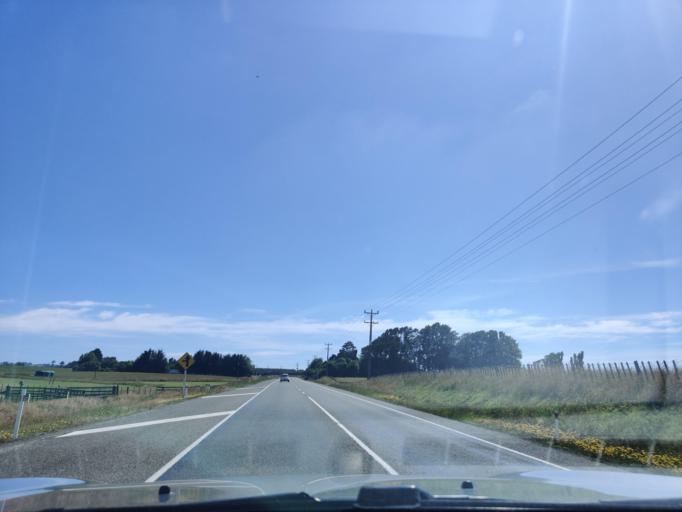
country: NZ
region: Manawatu-Wanganui
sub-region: Rangitikei District
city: Bulls
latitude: -40.0501
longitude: 175.4350
